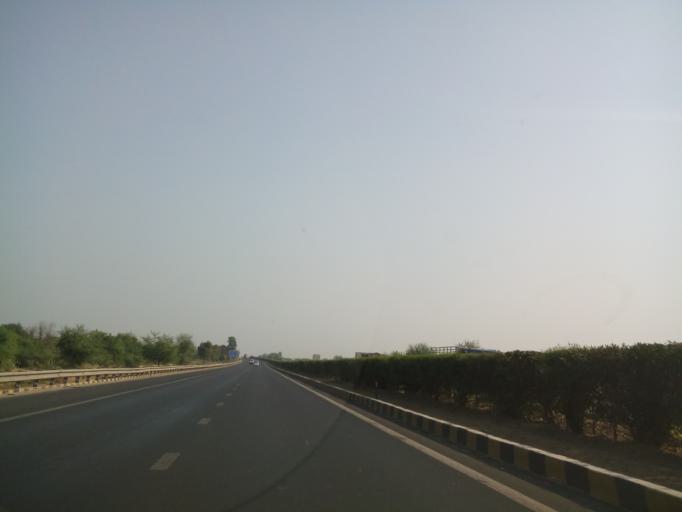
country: IN
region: Gujarat
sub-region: Ahmadabad
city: Ahmedabad
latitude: 22.9660
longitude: 72.6677
